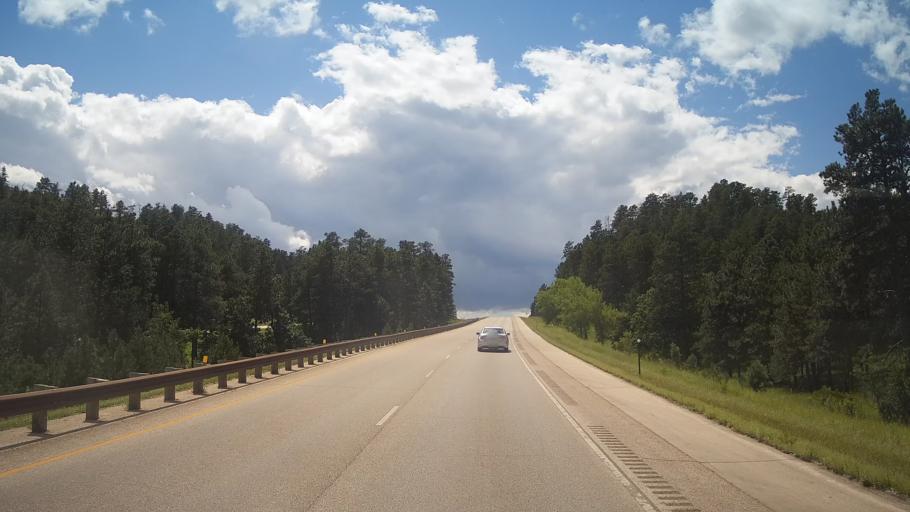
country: US
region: South Dakota
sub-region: Pennington County
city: Colonial Pine Hills
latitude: 43.9496
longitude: -103.3688
